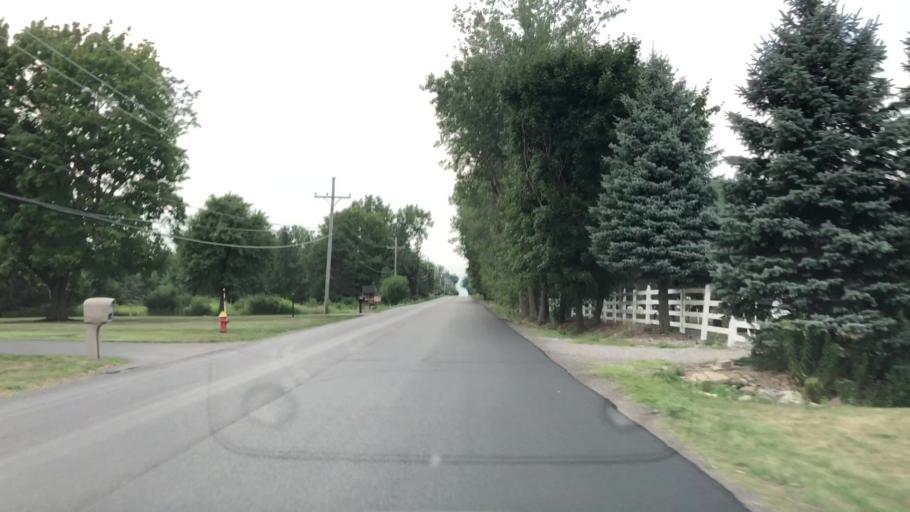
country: US
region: New York
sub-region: Erie County
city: Billington Heights
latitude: 42.8078
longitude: -78.6059
